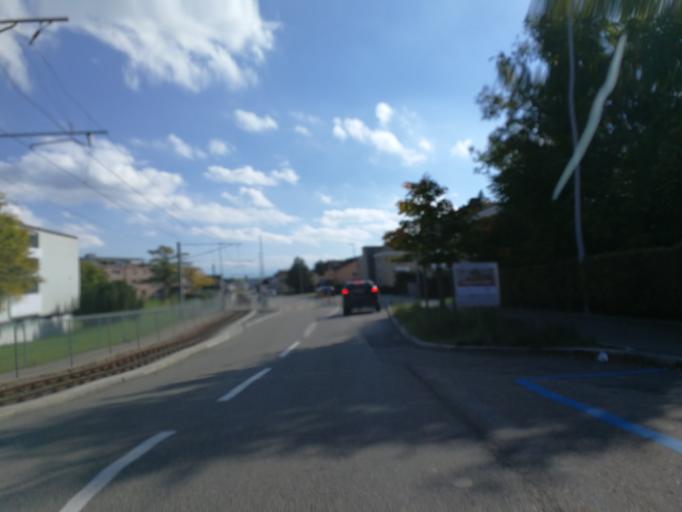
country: CH
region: Zurich
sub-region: Bezirk Uster
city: Egg
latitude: 47.2983
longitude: 8.6912
